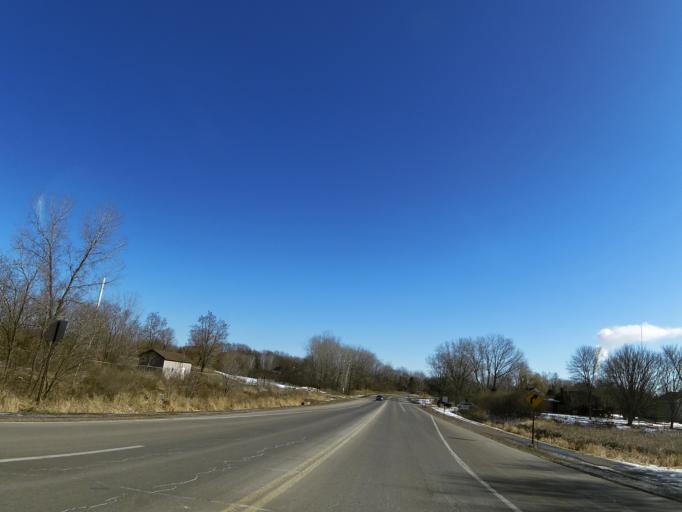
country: US
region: Minnesota
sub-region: Washington County
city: Stillwater
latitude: 45.0570
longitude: -92.8335
